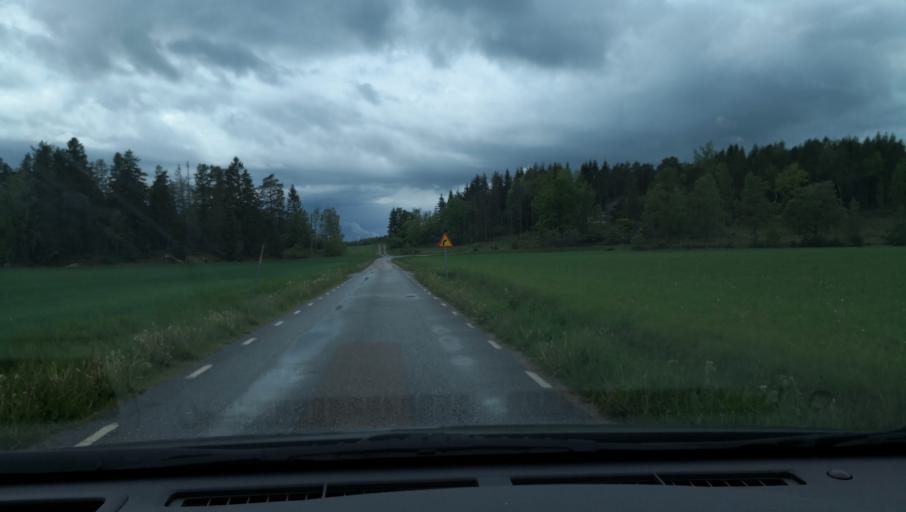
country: SE
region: Uppsala
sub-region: Enkopings Kommun
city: Orsundsbro
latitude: 59.7233
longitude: 17.3861
